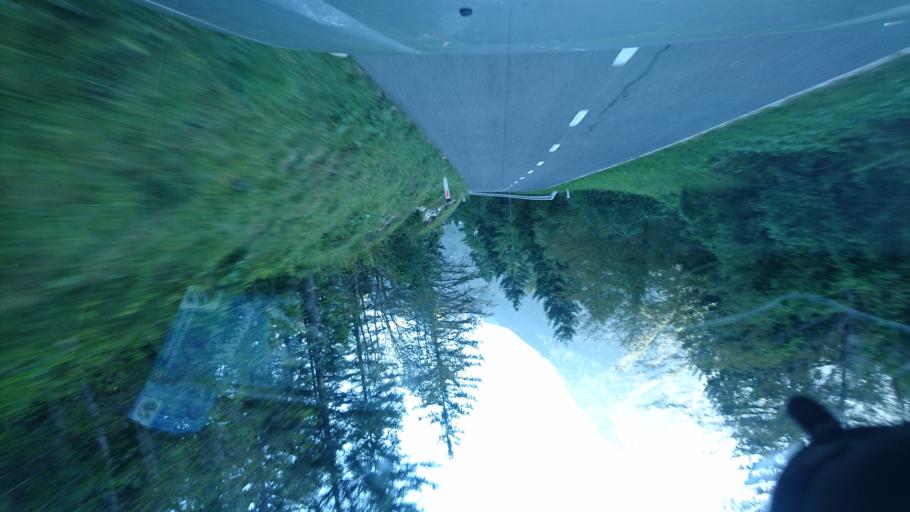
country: SI
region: Bovec
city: Bovec
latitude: 46.3746
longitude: 13.5842
